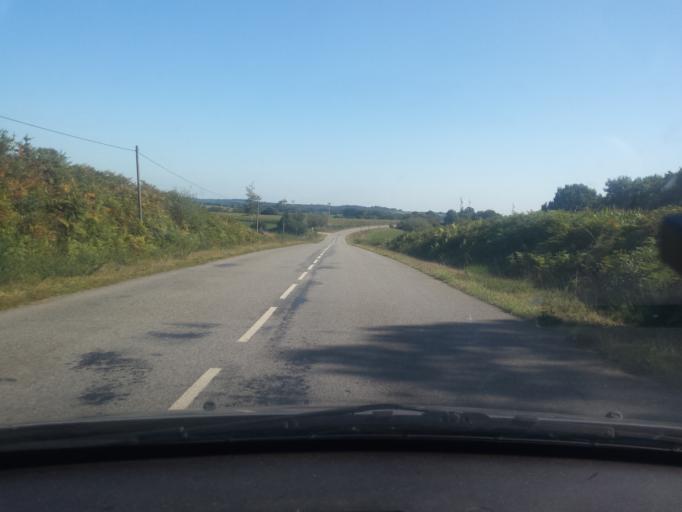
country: FR
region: Brittany
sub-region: Departement du Morbihan
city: Cleguerec
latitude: 48.1271
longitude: -3.1403
